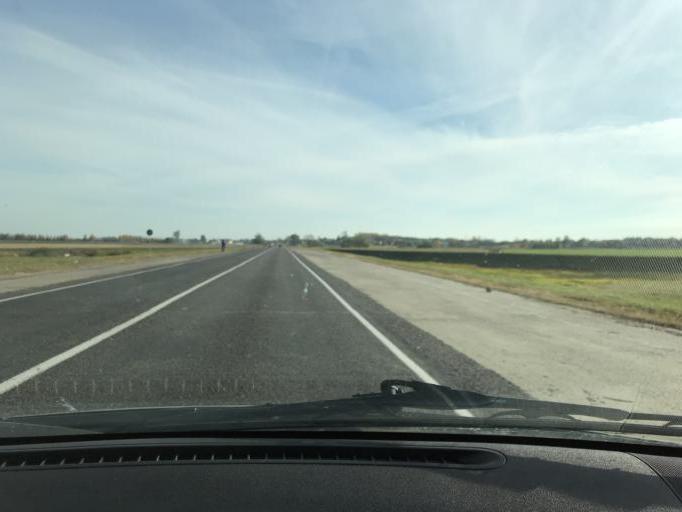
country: BY
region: Brest
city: Asnyezhytsy
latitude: 52.1837
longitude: 26.0809
